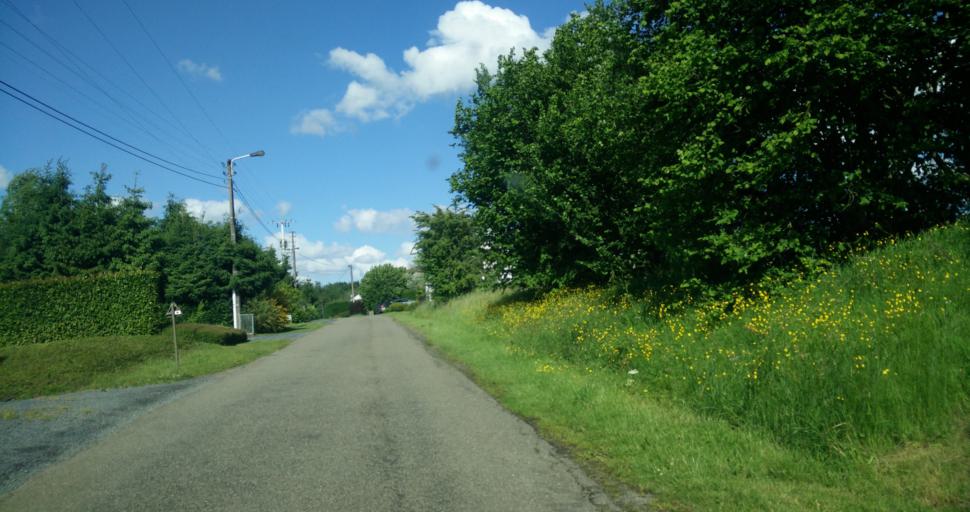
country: BE
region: Wallonia
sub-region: Province du Luxembourg
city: Houffalize
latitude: 50.1649
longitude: 5.7270
